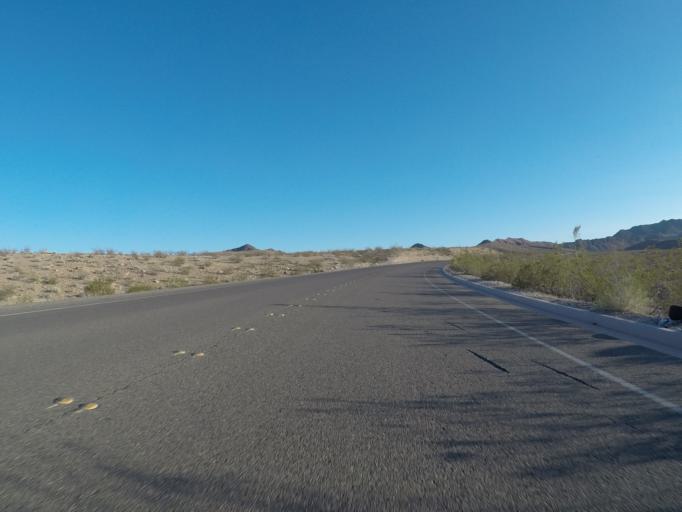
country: US
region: Nevada
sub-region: Clark County
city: Moapa Valley
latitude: 36.2740
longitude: -114.4834
